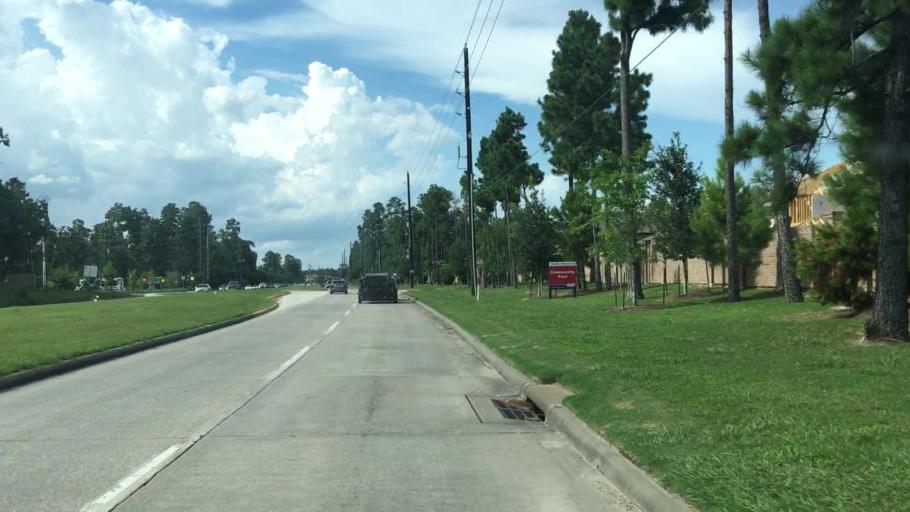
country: US
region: Texas
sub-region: Harris County
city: Atascocita
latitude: 29.9385
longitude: -95.1756
